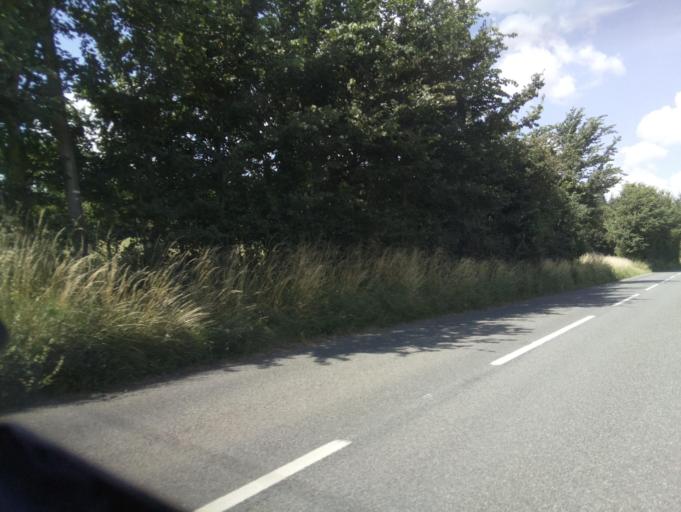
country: GB
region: England
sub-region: West Berkshire
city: Farnborough
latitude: 51.5040
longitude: -1.3651
